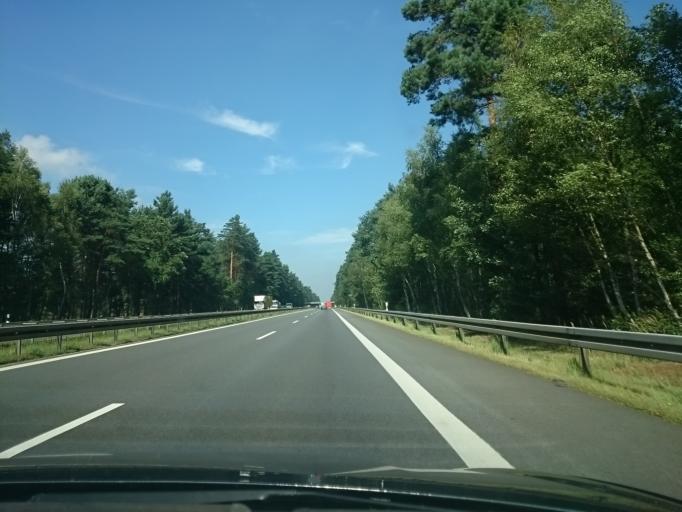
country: DE
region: Brandenburg
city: Bronkow
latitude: 51.7177
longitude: 13.8884
